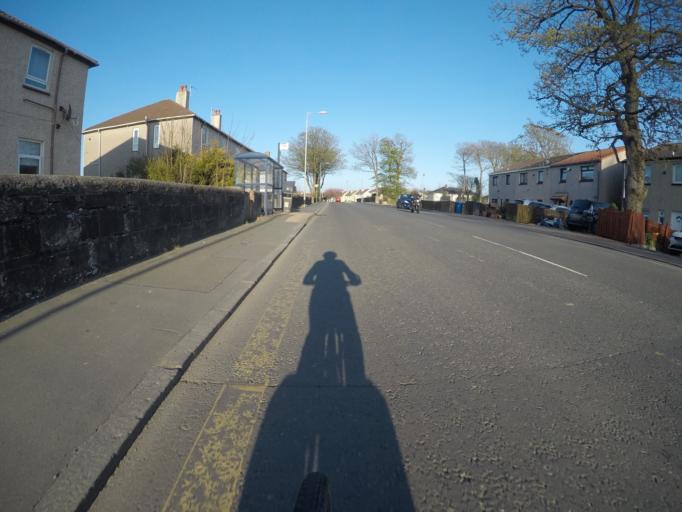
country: GB
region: Scotland
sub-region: North Ayrshire
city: Stevenston
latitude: 55.6416
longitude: -4.7516
